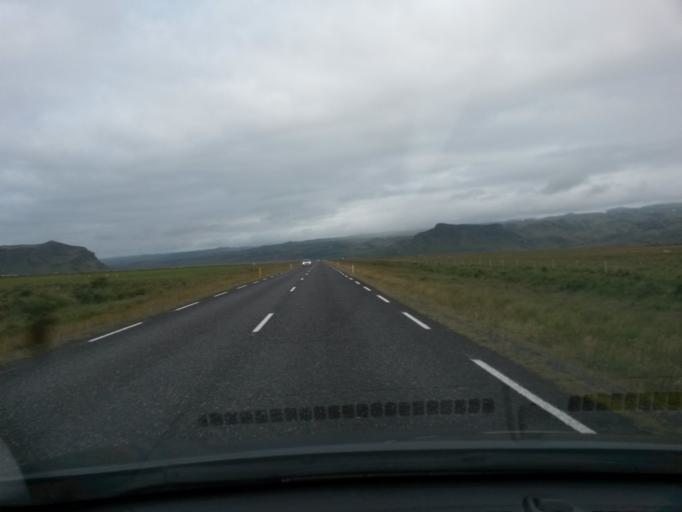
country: IS
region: South
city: Vestmannaeyjar
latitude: 63.4429
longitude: -19.1995
